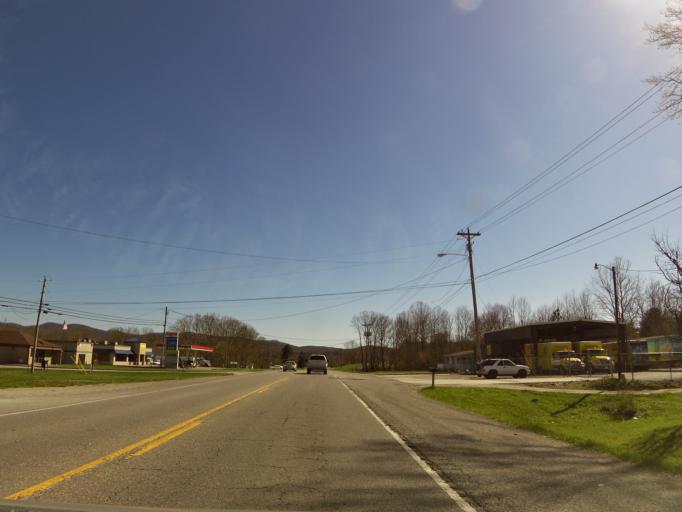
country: US
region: Tennessee
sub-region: Scott County
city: Oneida
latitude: 36.5596
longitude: -84.4502
